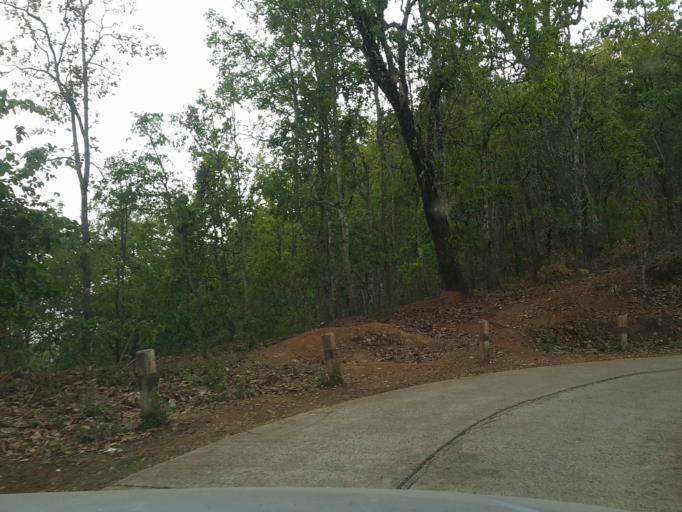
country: TH
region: Chiang Mai
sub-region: Amphoe Chiang Dao
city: Chiang Dao
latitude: 19.3837
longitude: 98.7715
